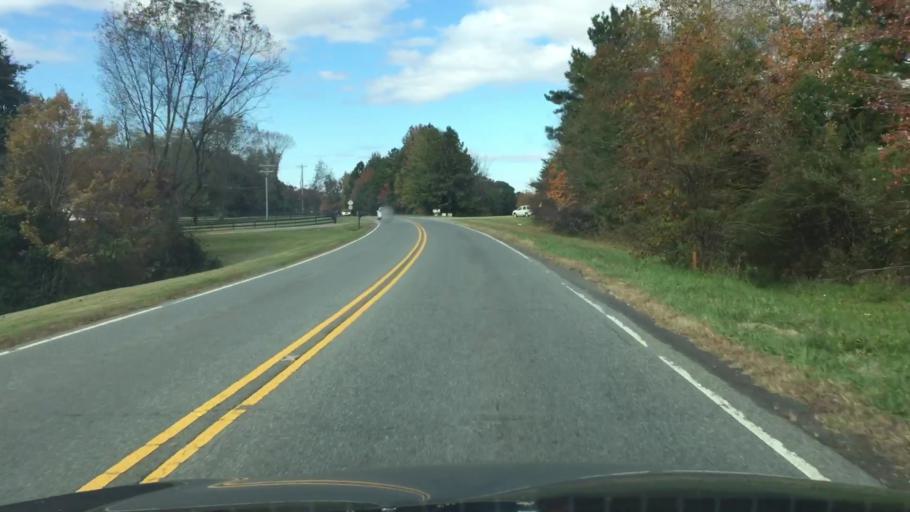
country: US
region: North Carolina
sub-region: Iredell County
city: Troutman
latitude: 35.6539
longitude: -80.8451
